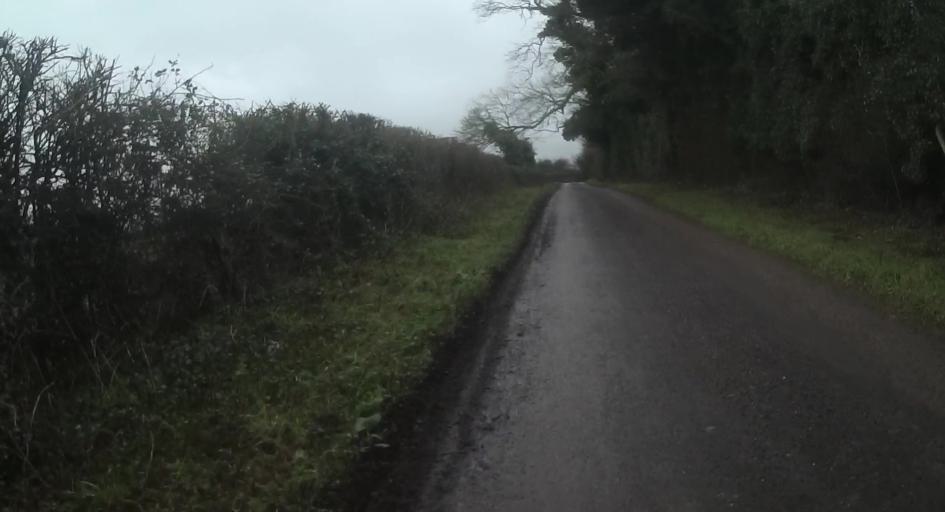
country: GB
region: England
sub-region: Hampshire
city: Kings Worthy
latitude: 51.1020
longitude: -1.2525
